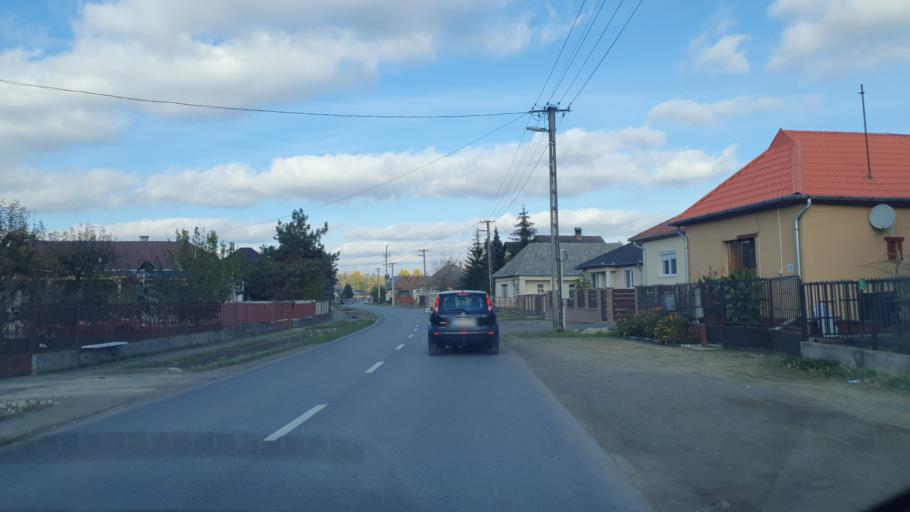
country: HU
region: Szabolcs-Szatmar-Bereg
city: Anarcs
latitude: 48.1694
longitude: 22.0971
